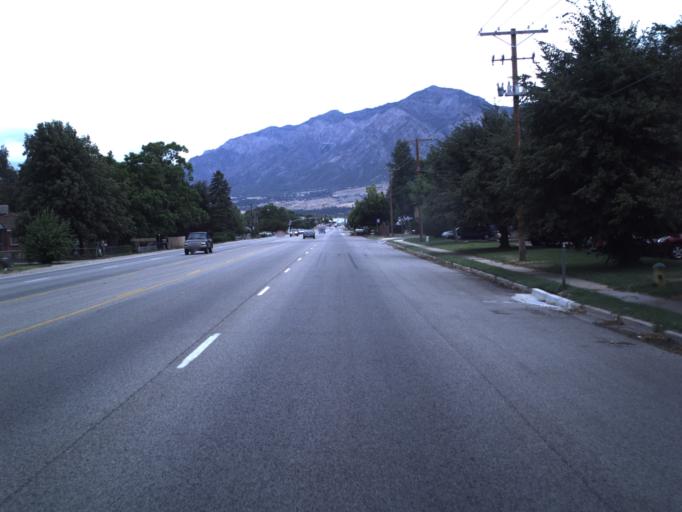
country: US
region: Utah
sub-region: Weber County
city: Harrisville
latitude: 41.2631
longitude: -111.9777
